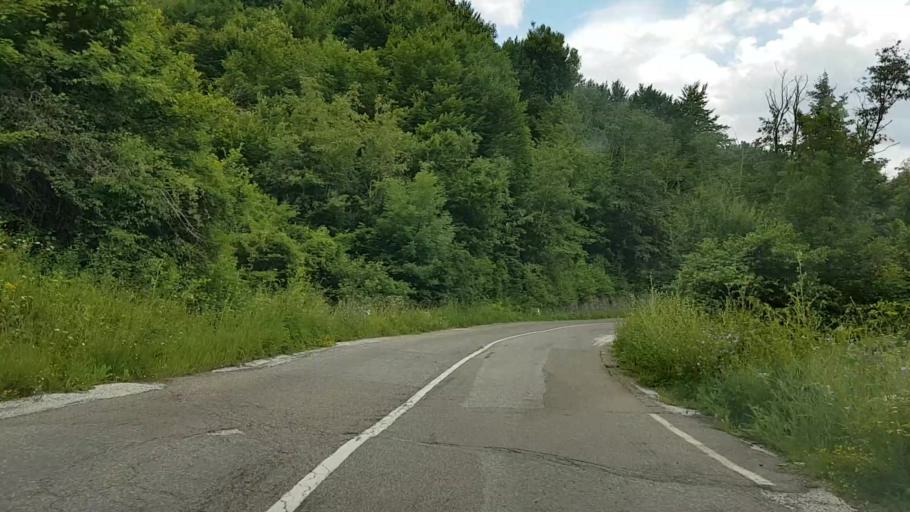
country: RO
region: Neamt
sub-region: Comuna Pangarati
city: Pangarati
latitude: 46.9575
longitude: 26.1251
